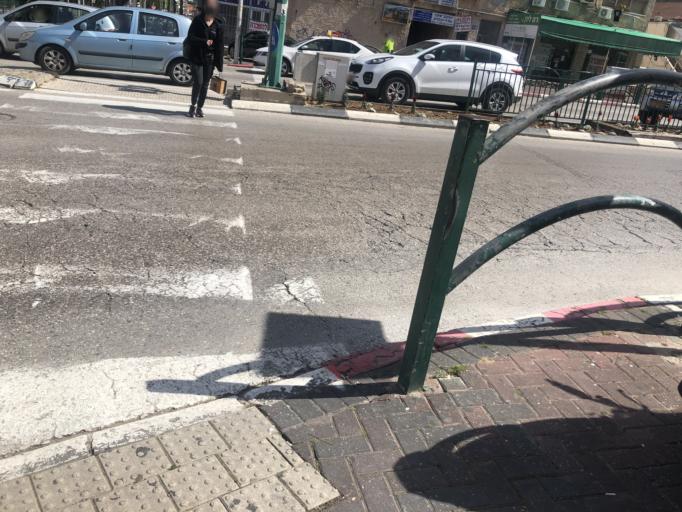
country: IL
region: Haifa
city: Hadera
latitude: 32.4386
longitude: 34.9234
